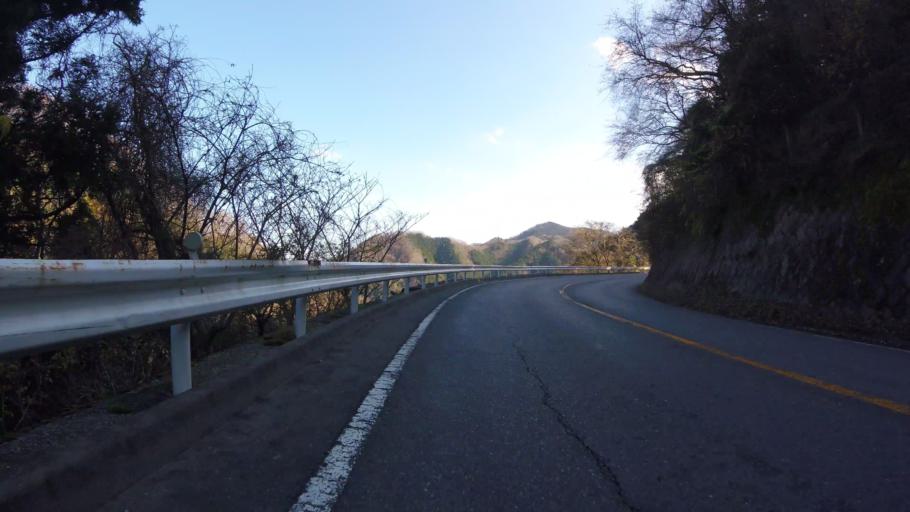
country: JP
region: Shizuoka
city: Ito
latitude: 34.9315
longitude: 139.0552
